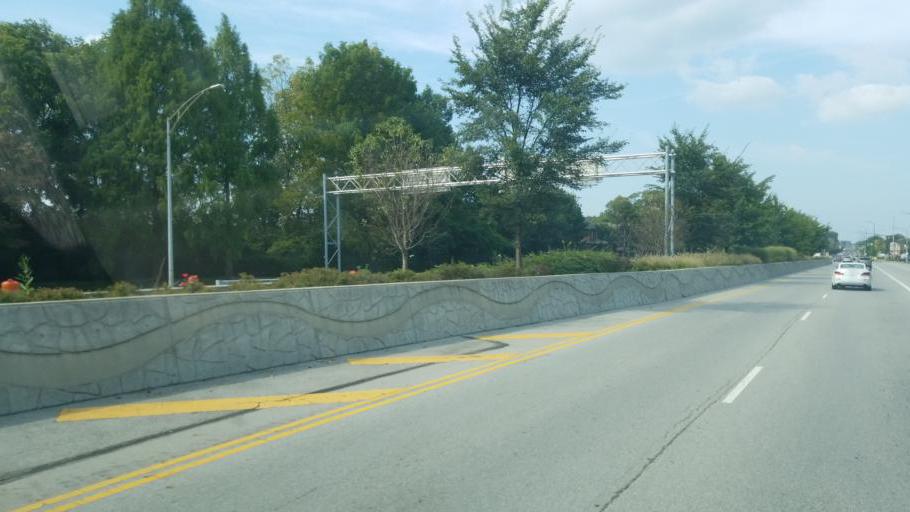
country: US
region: Ohio
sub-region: Franklin County
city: Gahanna
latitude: 40.0069
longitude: -82.8674
